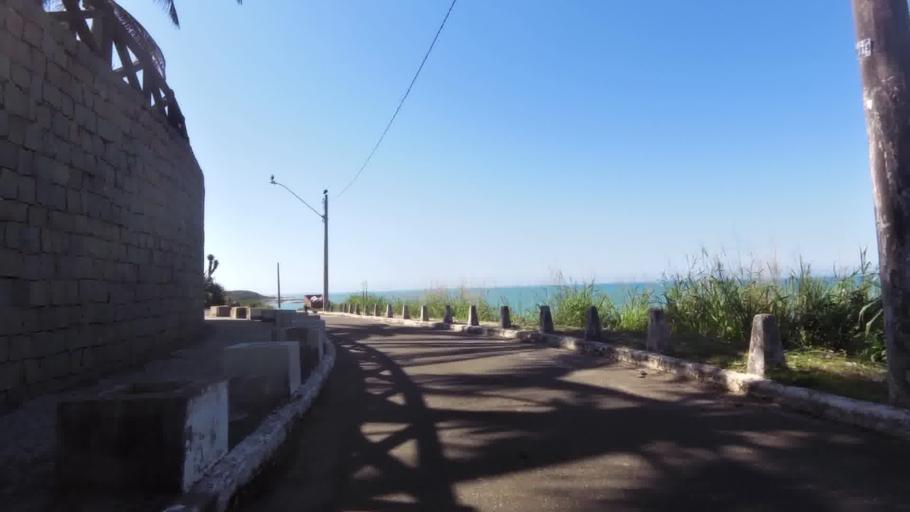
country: BR
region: Espirito Santo
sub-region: Guarapari
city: Guarapari
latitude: -20.7442
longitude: -40.5367
